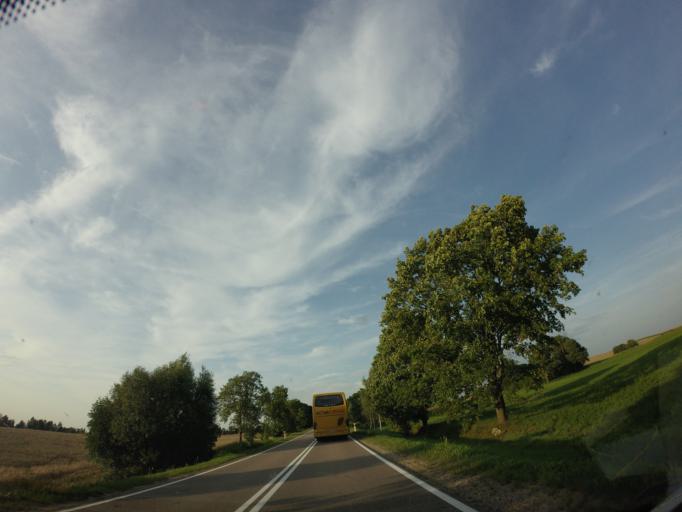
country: PL
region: Podlasie
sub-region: Powiat sejnenski
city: Sejny
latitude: 54.1020
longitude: 23.4036
